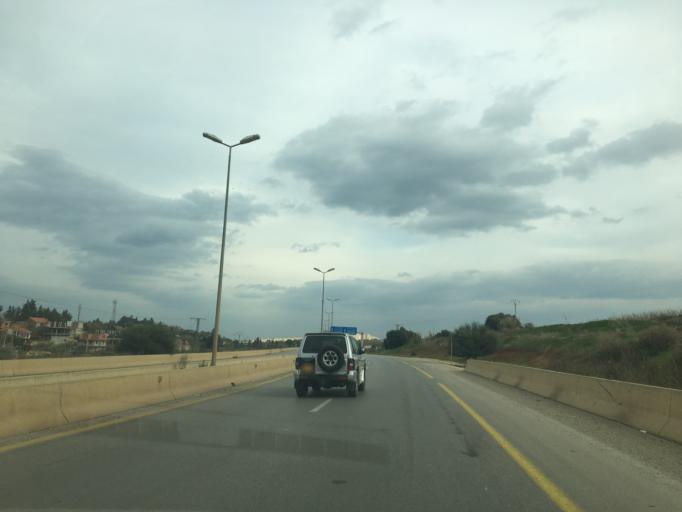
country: DZ
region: Tipaza
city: Tipasa
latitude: 36.5716
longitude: 2.4165
